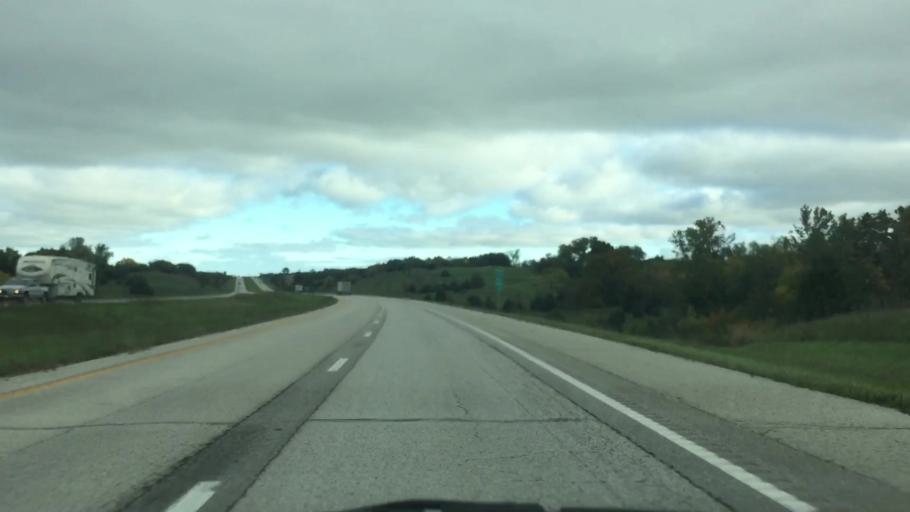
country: US
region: Missouri
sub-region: Harrison County
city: Bethany
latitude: 40.1805
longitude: -94.0151
